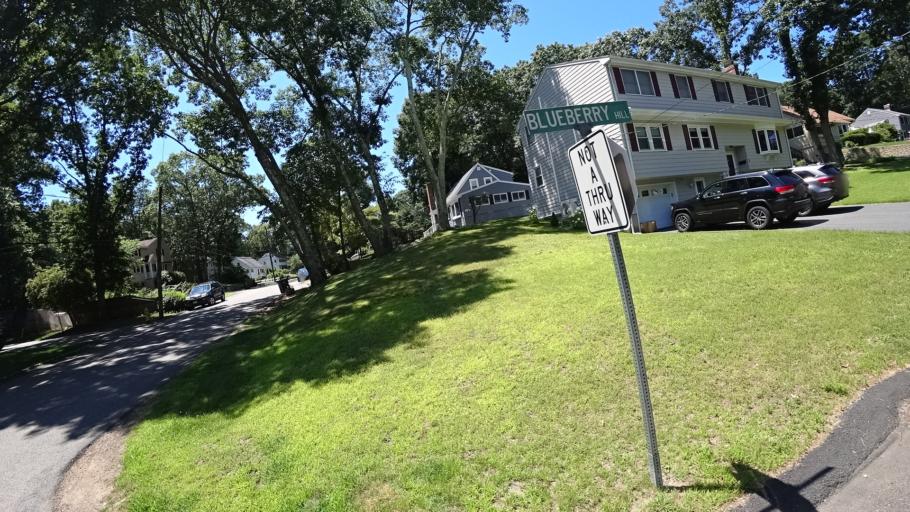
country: US
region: Massachusetts
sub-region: Norfolk County
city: Dedham
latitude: 42.2261
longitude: -71.1581
